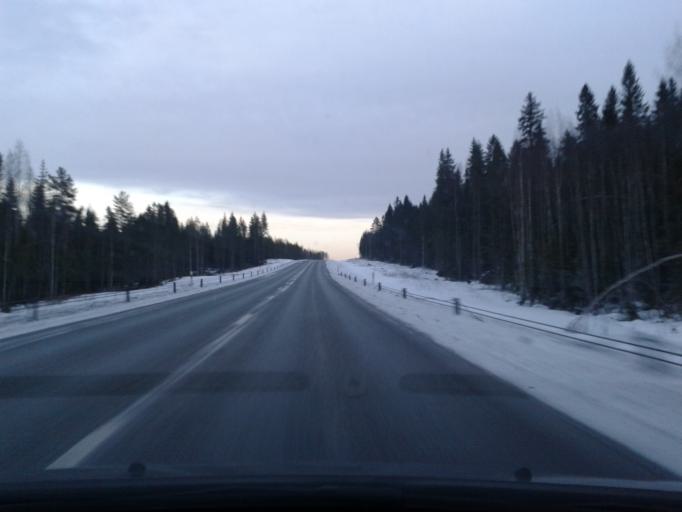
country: SE
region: Vaesternorrland
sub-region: Kramfors Kommun
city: Bollstabruk
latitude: 63.0619
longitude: 17.5981
